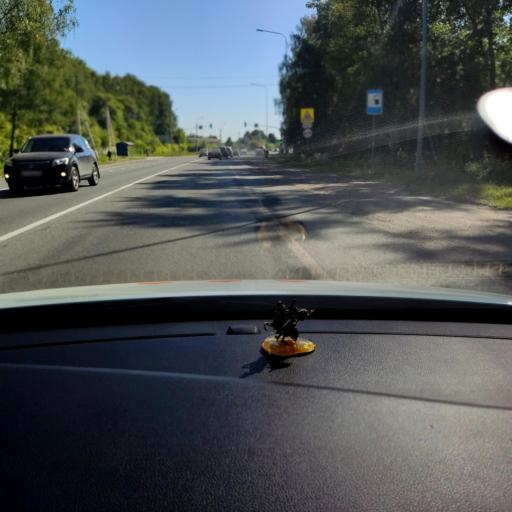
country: RU
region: Tatarstan
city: Aysha
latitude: 55.8704
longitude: 48.6248
